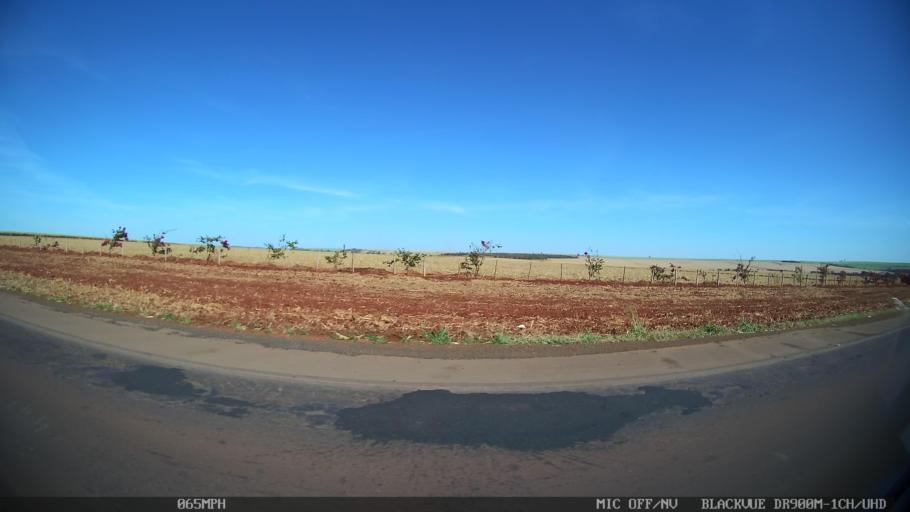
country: BR
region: Sao Paulo
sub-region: Ipua
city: Ipua
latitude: -20.4954
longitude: -47.9751
